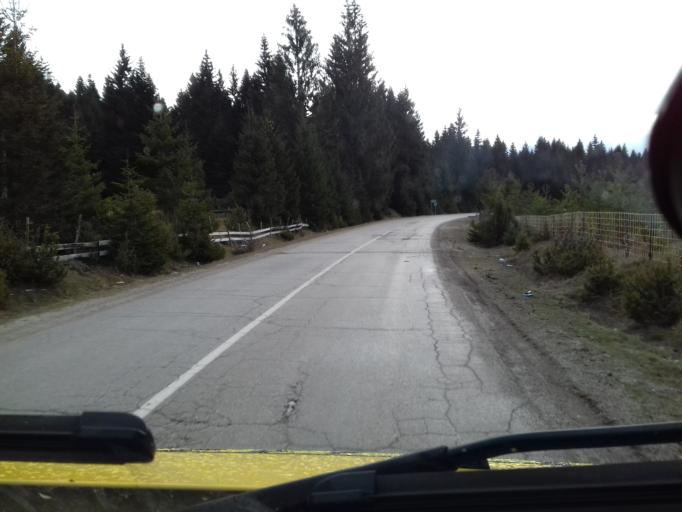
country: BA
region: Federation of Bosnia and Herzegovina
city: Turbe
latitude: 44.2934
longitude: 17.5017
